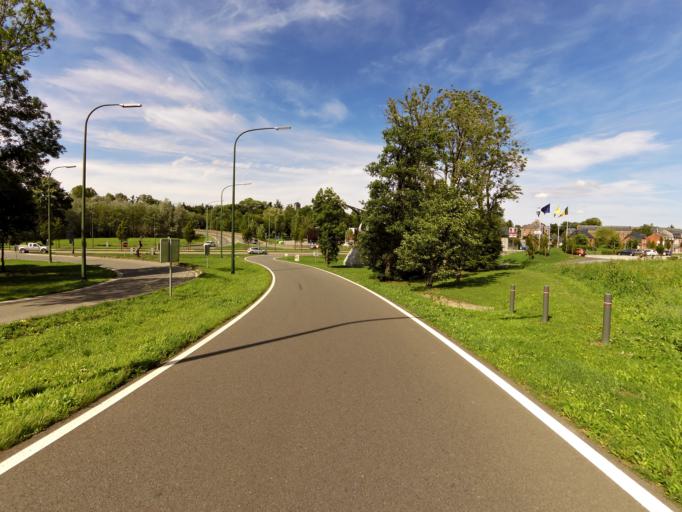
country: BE
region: Wallonia
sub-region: Province du Luxembourg
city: Marche-en-Famenne
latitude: 50.2250
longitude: 5.3391
